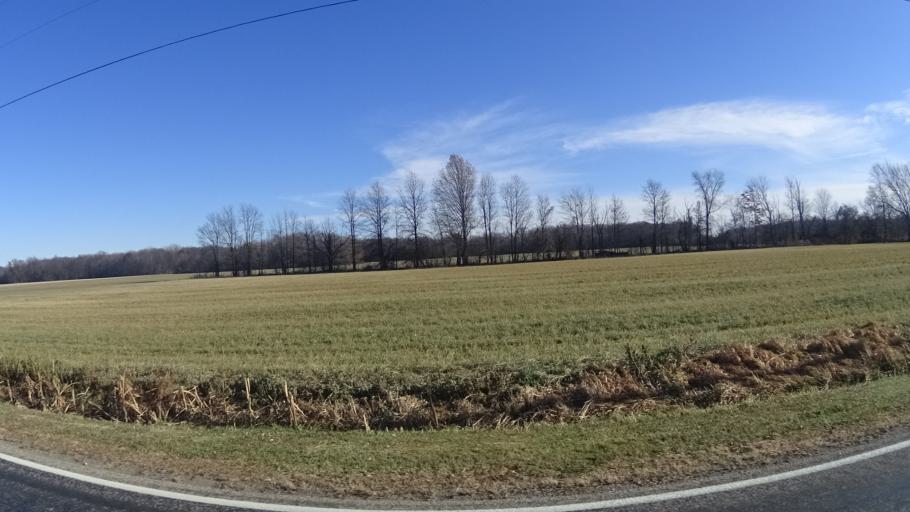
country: US
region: Ohio
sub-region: Lorain County
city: South Amherst
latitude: 41.3310
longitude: -82.2881
